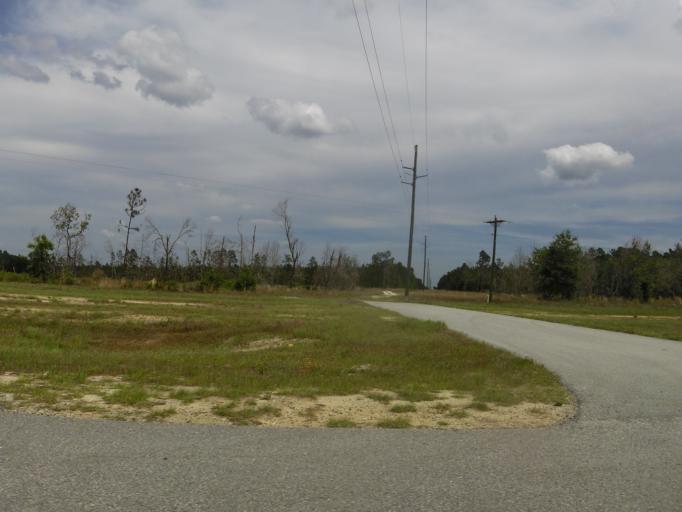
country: US
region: Georgia
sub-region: Emanuel County
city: Swainsboro
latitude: 32.6763
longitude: -82.3859
